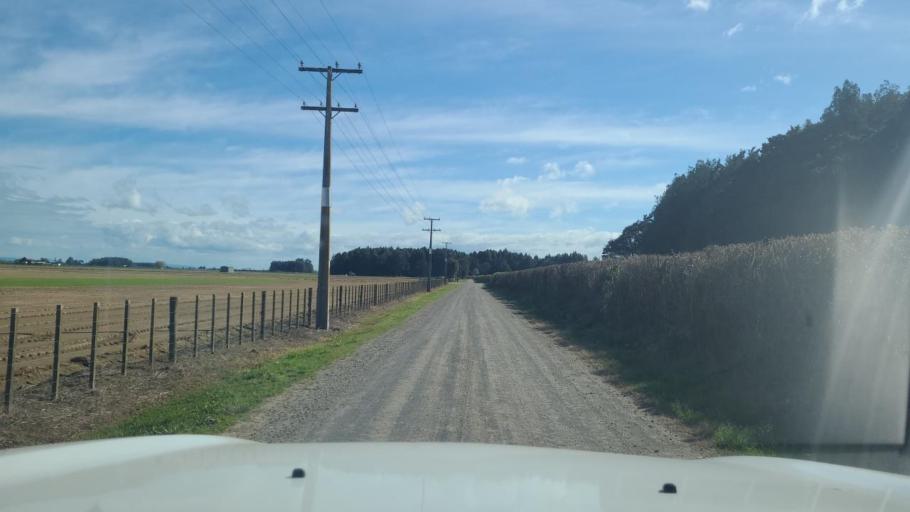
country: NZ
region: Waikato
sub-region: Matamata-Piako District
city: Matamata
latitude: -37.7374
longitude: 175.7546
